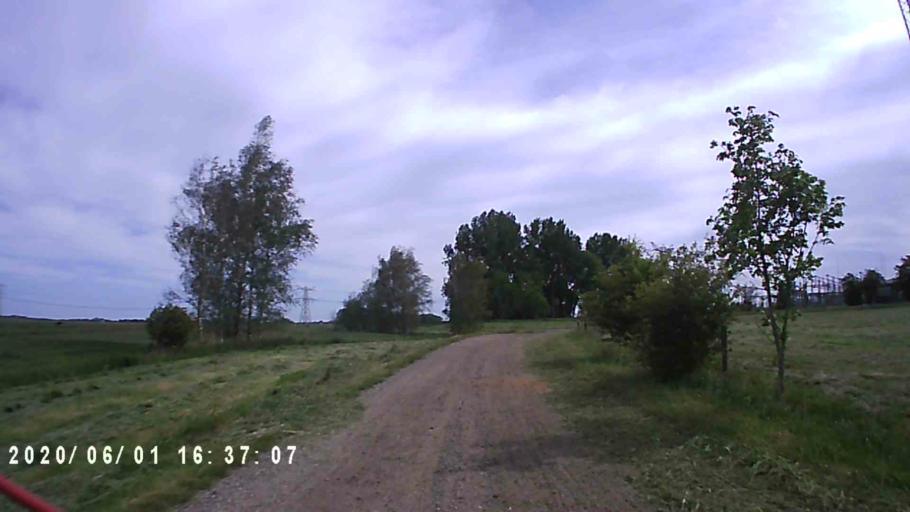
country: NL
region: Friesland
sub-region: Gemeente Tytsjerksteradiel
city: Tytsjerk
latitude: 53.1912
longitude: 5.8776
